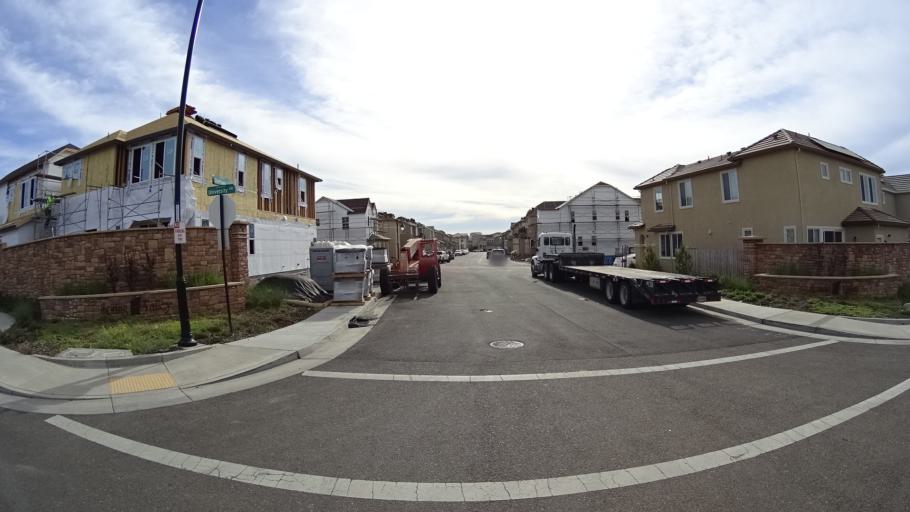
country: US
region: California
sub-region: Placer County
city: Lincoln
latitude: 38.8274
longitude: -121.2949
